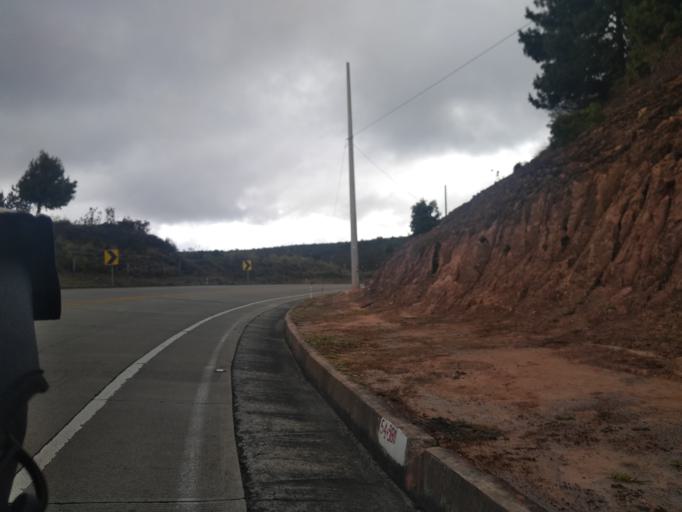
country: EC
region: Azuay
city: Cuenca
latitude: -3.3675
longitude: -79.1949
